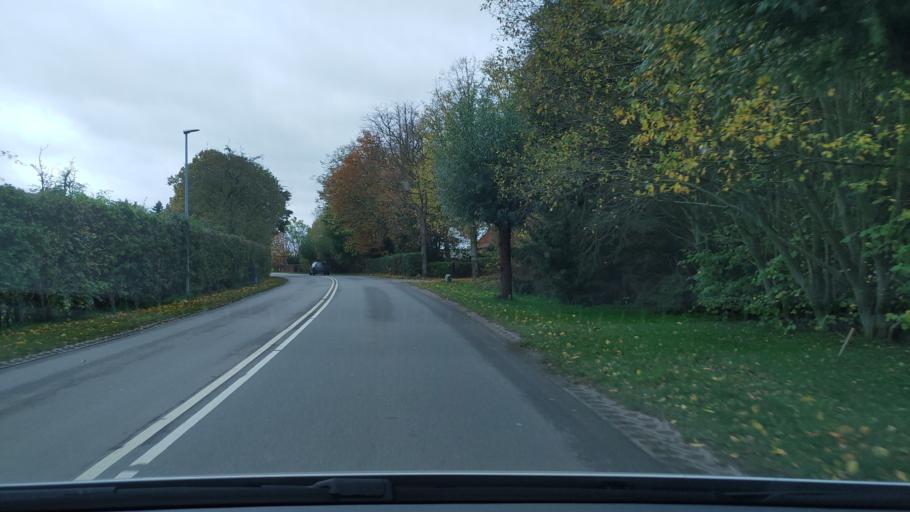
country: DK
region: Capital Region
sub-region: Tarnby Kommune
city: Tarnby
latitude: 55.6049
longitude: 12.6060
